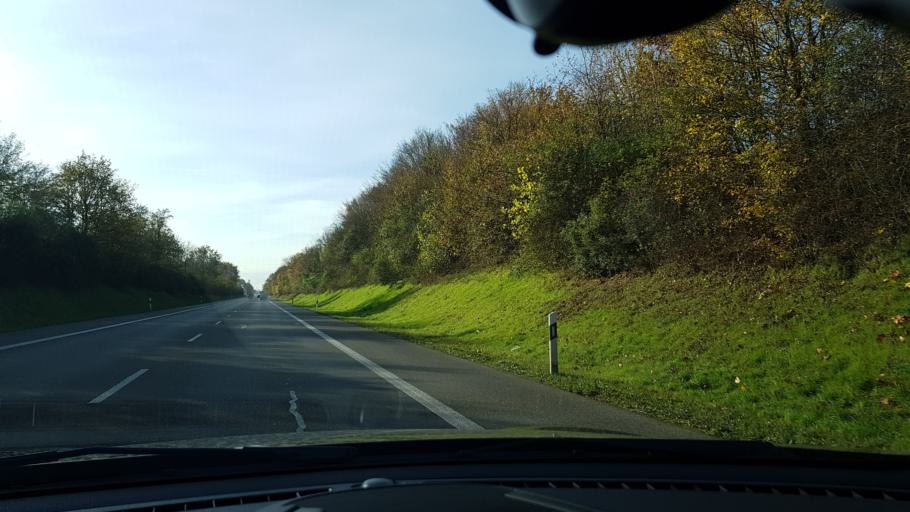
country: DE
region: North Rhine-Westphalia
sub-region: Regierungsbezirk Dusseldorf
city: Neubrueck
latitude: 51.1008
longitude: 6.6241
